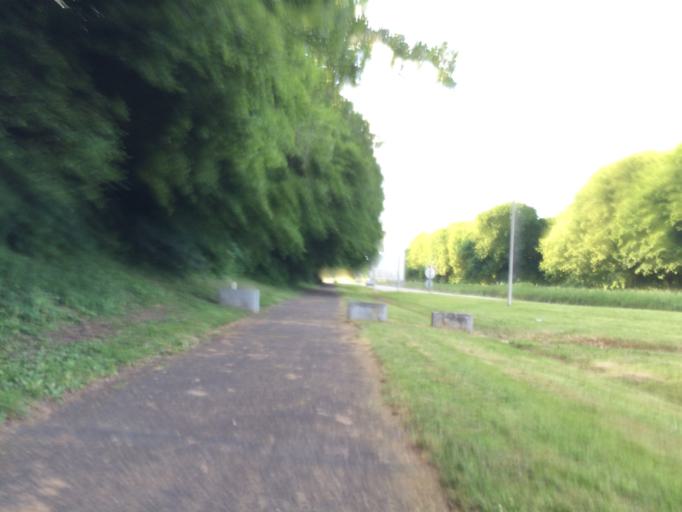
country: FR
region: Ile-de-France
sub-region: Departement de l'Essonne
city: Lisses
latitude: 48.6149
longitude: 2.4227
